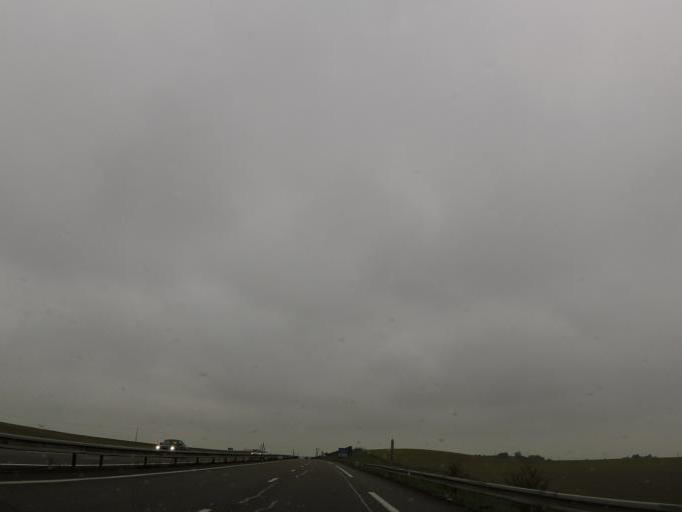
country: FR
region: Champagne-Ardenne
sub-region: Departement de la Marne
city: Sainte-Menehould
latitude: 49.0766
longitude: 4.8112
